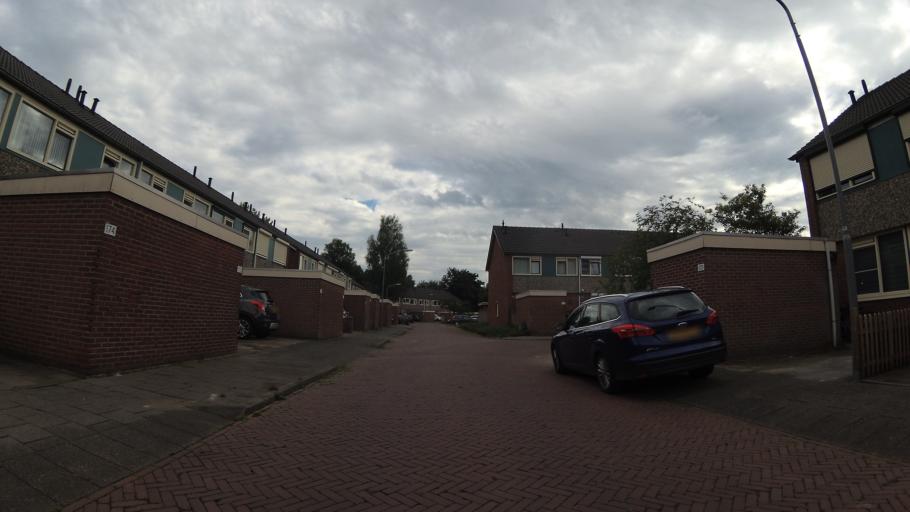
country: NL
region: North Brabant
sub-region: Gemeente Made en Drimmelen
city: Made
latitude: 51.6700
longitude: 4.7833
